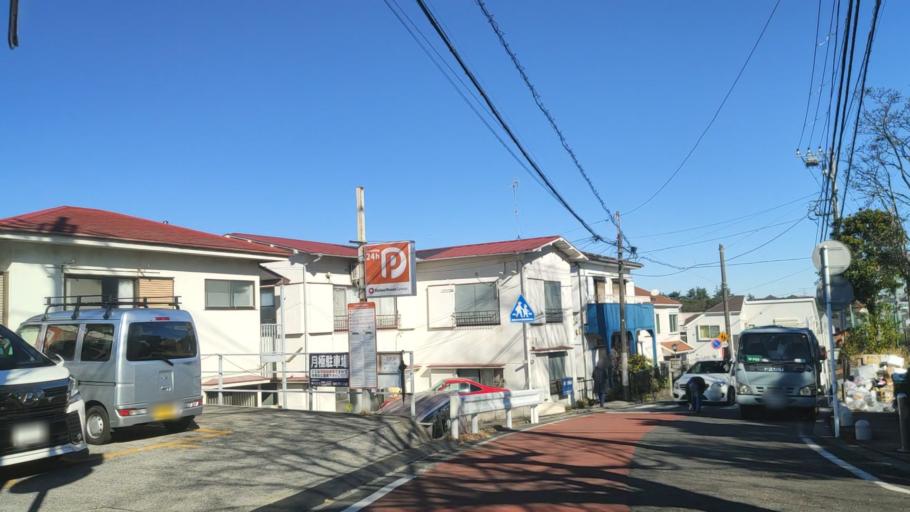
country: JP
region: Kanagawa
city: Yokohama
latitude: 35.4312
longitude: 139.6451
